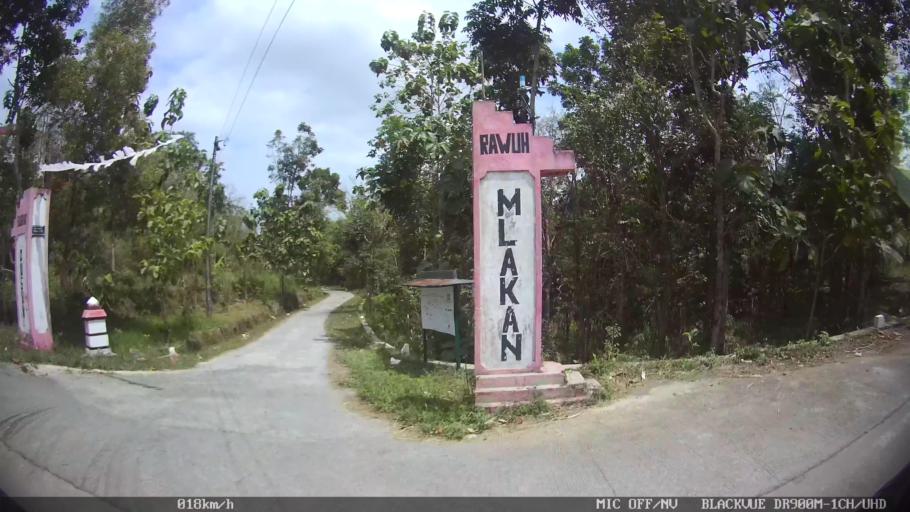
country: ID
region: Central Java
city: Candi Prambanan
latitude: -7.7905
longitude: 110.5187
